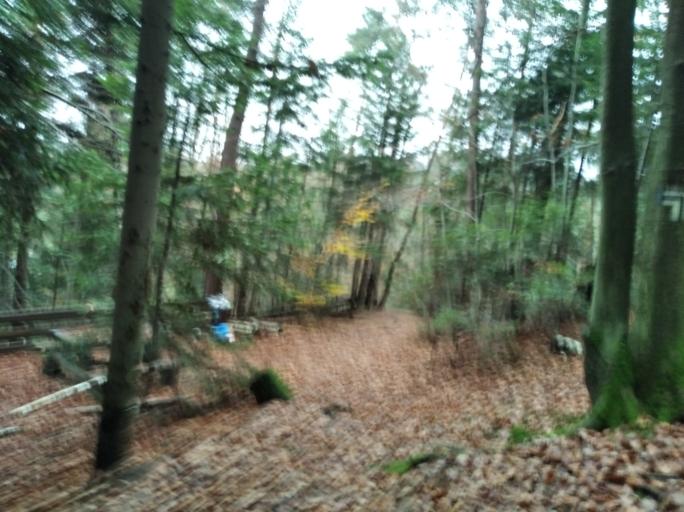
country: PL
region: Subcarpathian Voivodeship
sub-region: Powiat krosnienski
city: Korczyna
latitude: 49.7408
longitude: 21.7941
